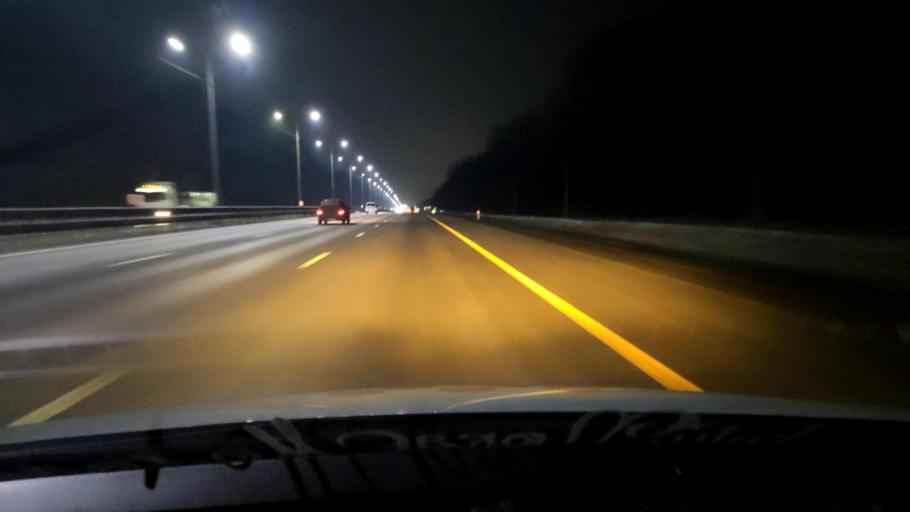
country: RU
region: Voronezj
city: Ramon'
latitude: 51.8616
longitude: 39.2156
